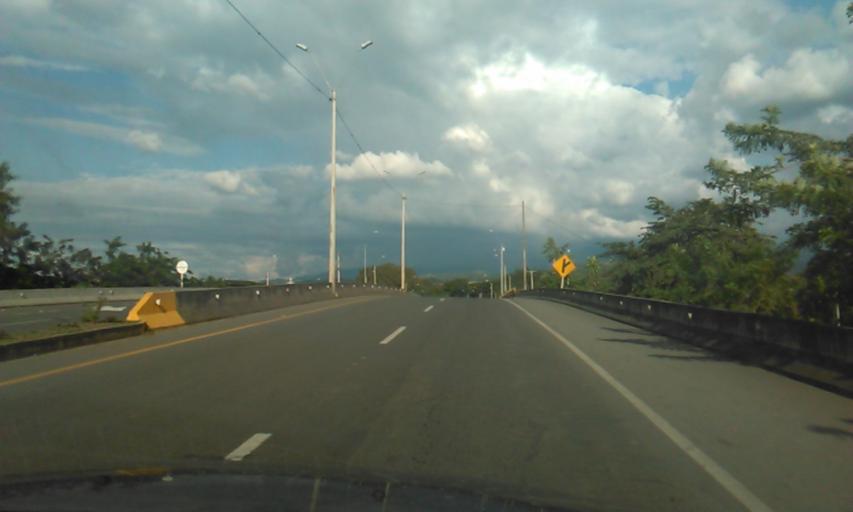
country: CO
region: Valle del Cauca
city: Buga
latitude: 3.8931
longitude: -76.3130
